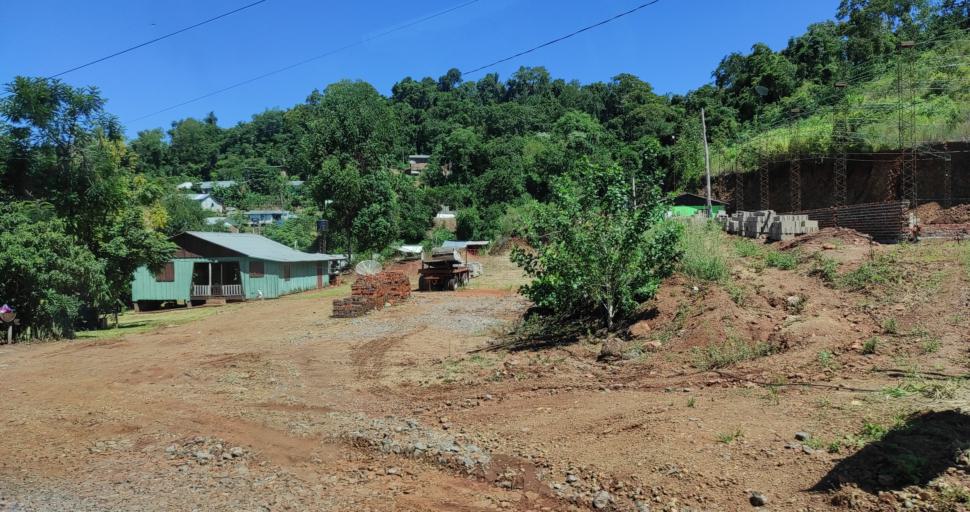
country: AR
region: Misiones
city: El Soberbio
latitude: -27.2887
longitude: -54.2119
